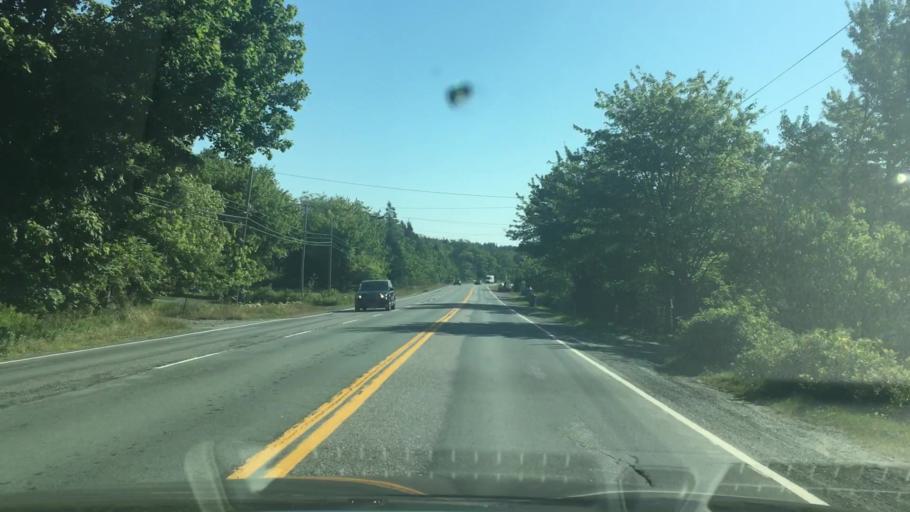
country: CA
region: Nova Scotia
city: Cole Harbour
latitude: 44.7787
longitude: -63.0837
